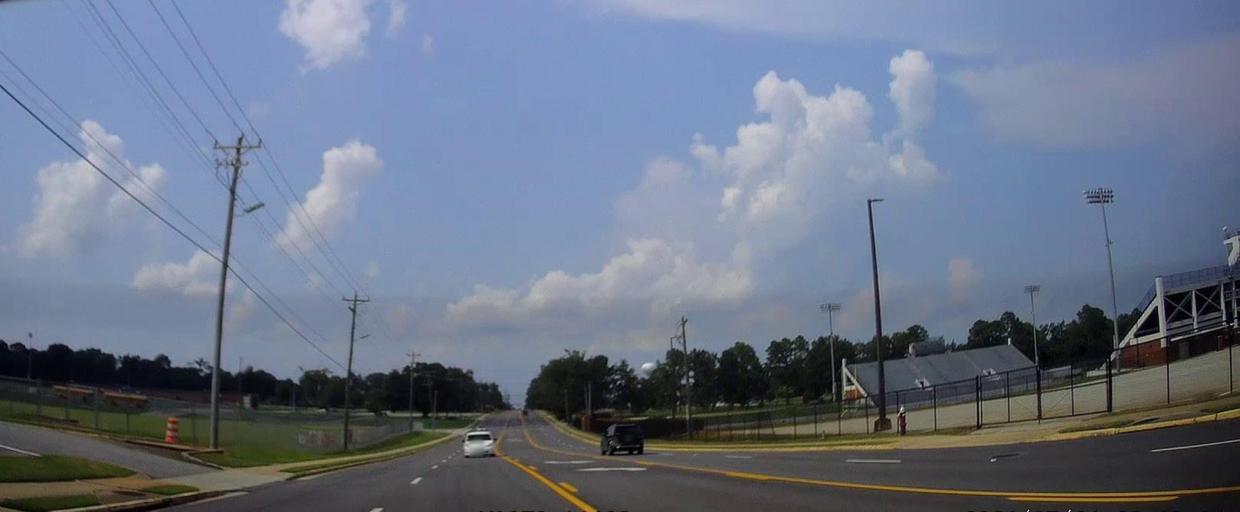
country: US
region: Georgia
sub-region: Houston County
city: Warner Robins
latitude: 32.6107
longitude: -83.6132
